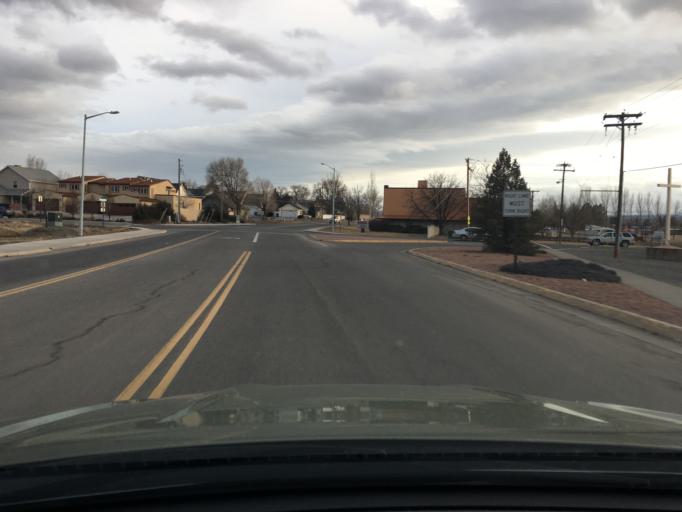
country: US
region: Colorado
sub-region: Montrose County
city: Montrose
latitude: 38.4824
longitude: -107.8570
